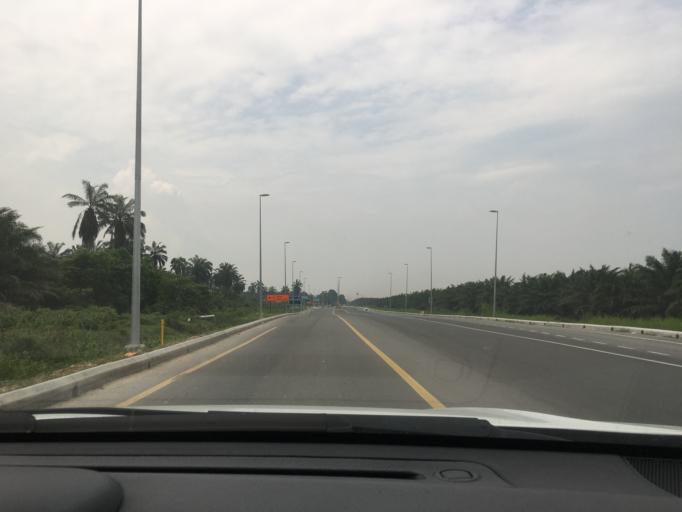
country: MY
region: Selangor
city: Klang
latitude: 3.1362
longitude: 101.3999
